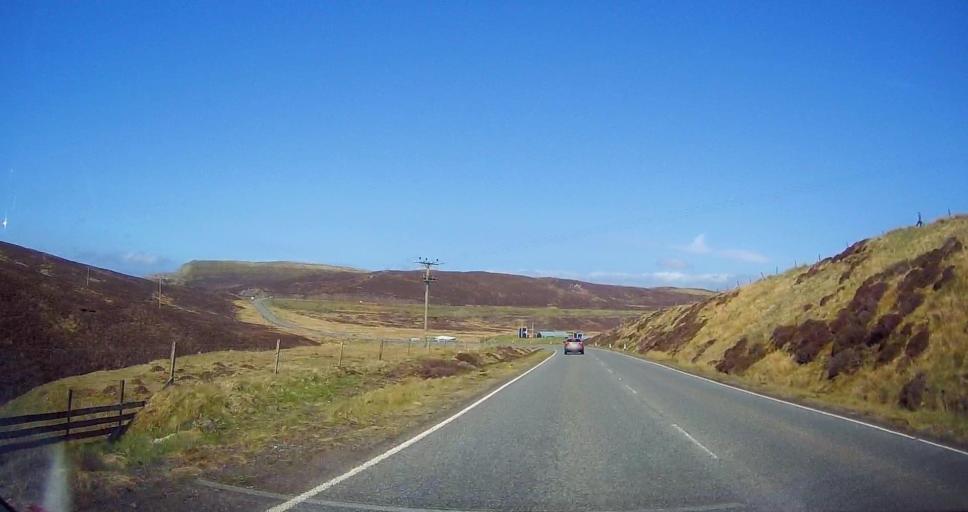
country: GB
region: Scotland
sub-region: Shetland Islands
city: Lerwick
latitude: 60.1388
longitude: -1.2342
